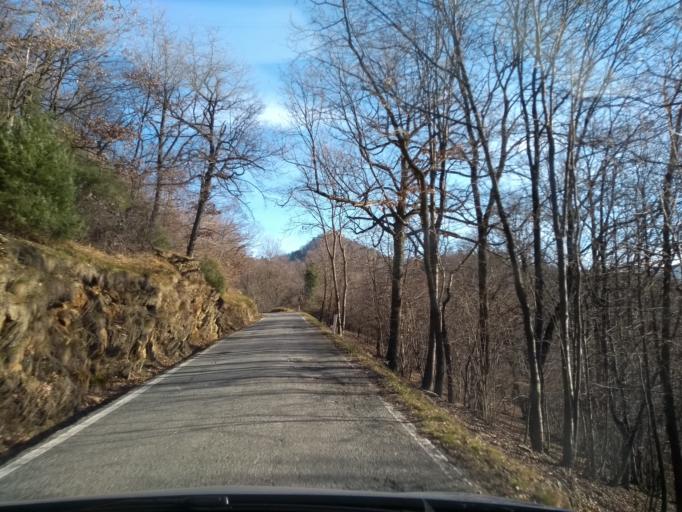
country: IT
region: Piedmont
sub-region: Provincia di Torino
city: Pessinetto
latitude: 45.2824
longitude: 7.4274
